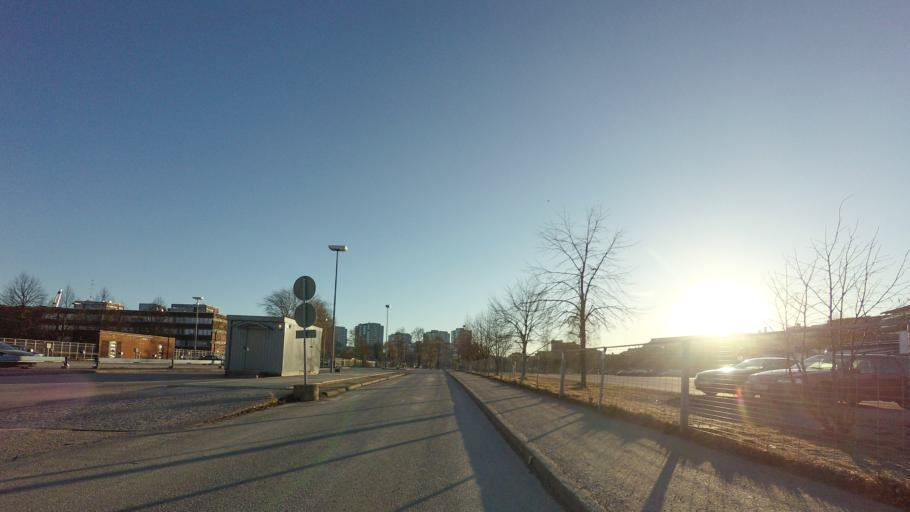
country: FI
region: Uusimaa
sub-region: Helsinki
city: Helsinki
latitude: 60.1839
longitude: 24.9677
